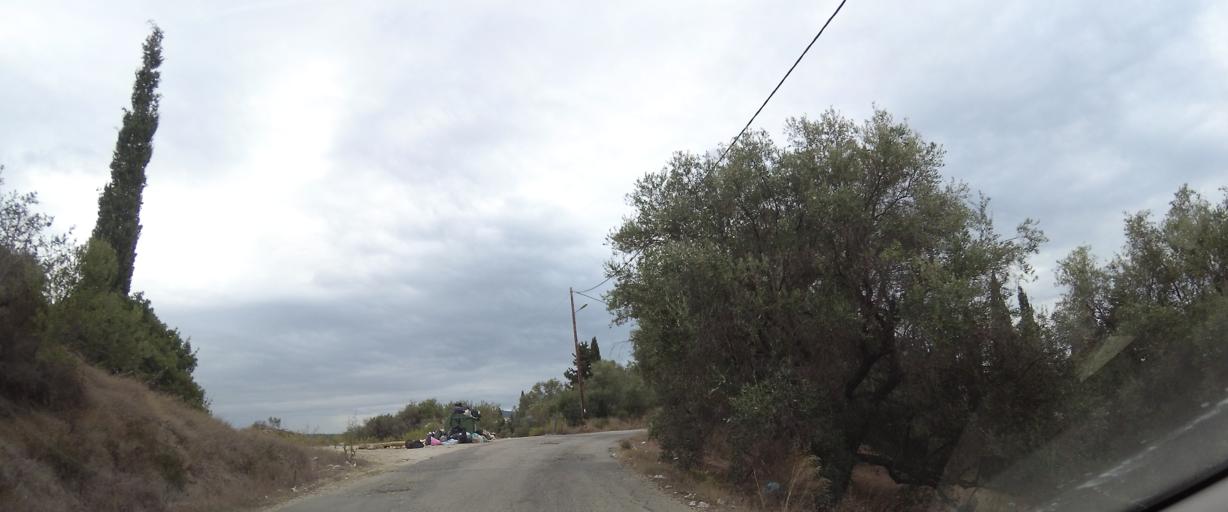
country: GR
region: Ionian Islands
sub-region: Nomos Kerkyras
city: Agios Georgis
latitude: 39.7428
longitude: 19.6784
